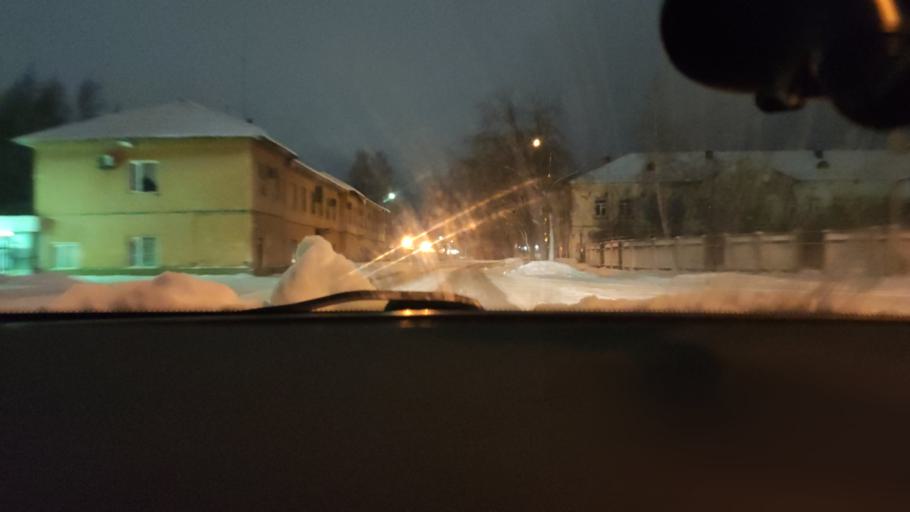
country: RU
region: Perm
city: Krasnokamsk
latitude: 58.0781
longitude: 55.7755
